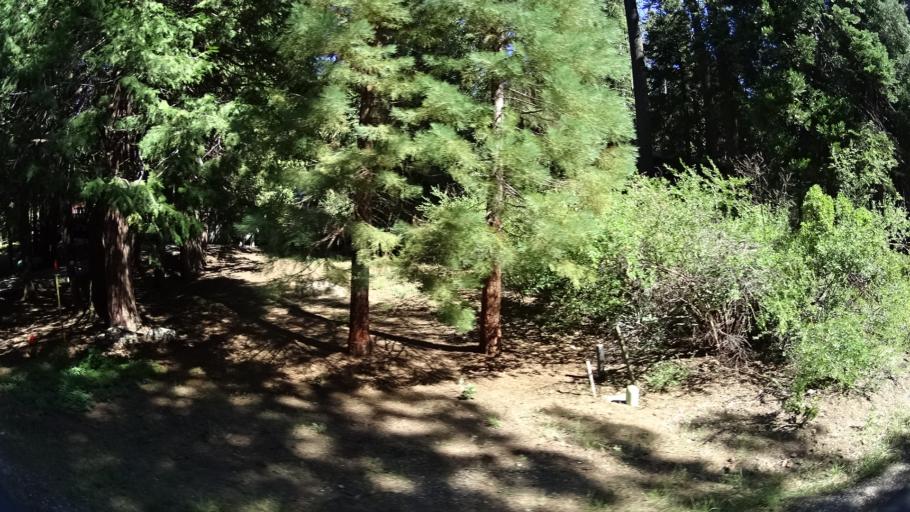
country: US
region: California
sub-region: Calaveras County
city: Arnold
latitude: 38.2932
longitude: -120.2803
